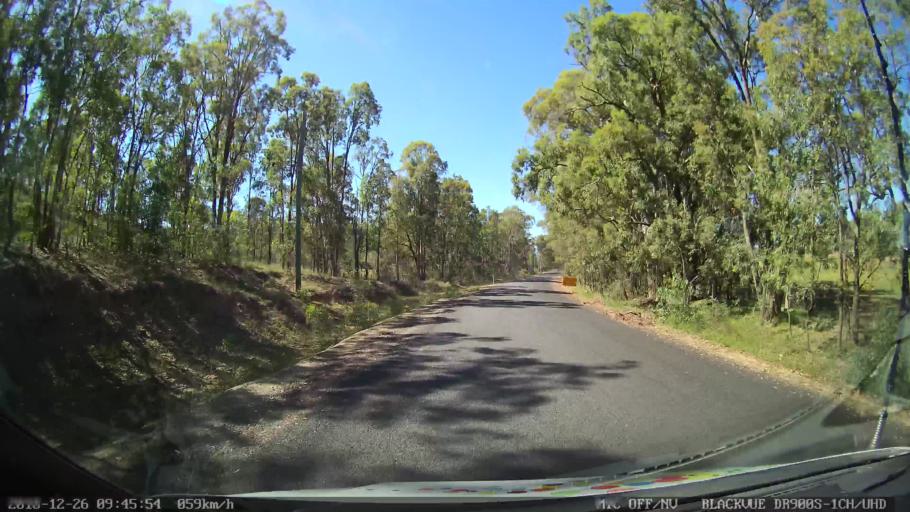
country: AU
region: New South Wales
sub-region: Mid-Western Regional
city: Kandos
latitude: -32.9648
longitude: 150.1061
